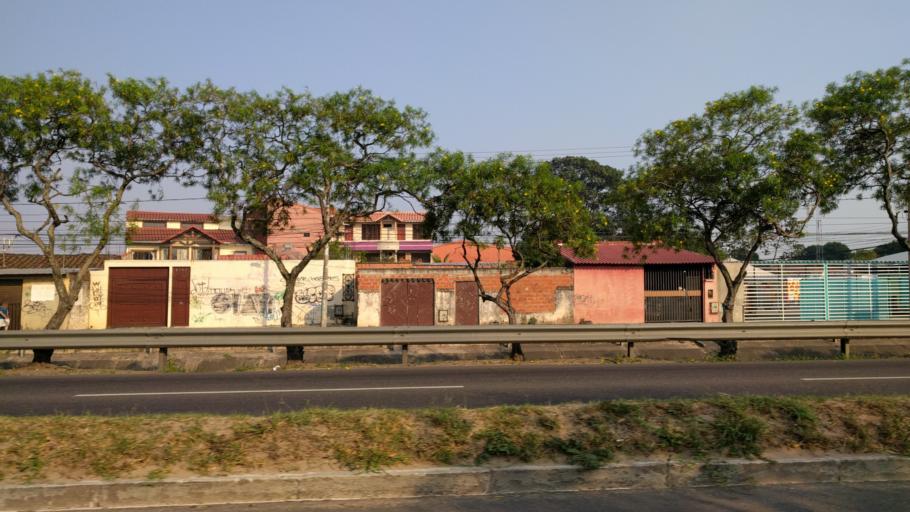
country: BO
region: Santa Cruz
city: Santa Cruz de la Sierra
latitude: -17.7822
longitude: -63.1944
